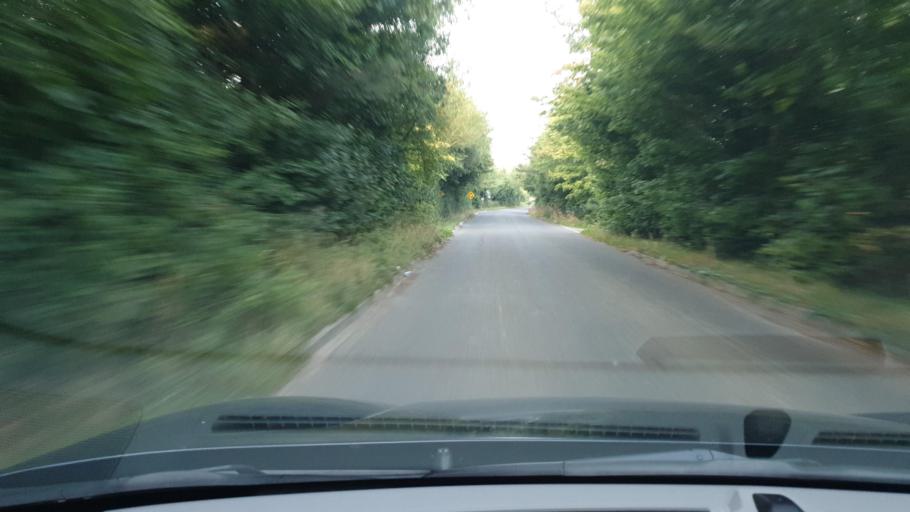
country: IE
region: Leinster
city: Balrothery
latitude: 53.5620
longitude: -6.2207
